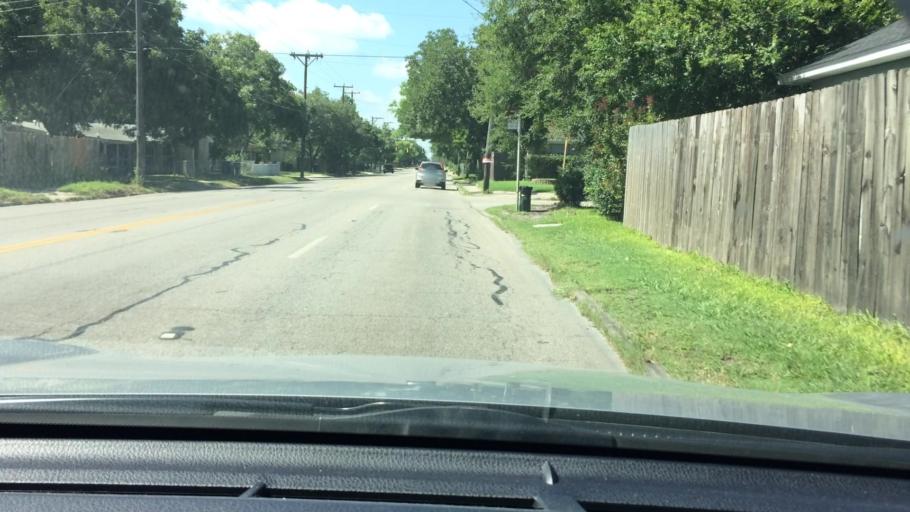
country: US
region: Texas
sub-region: Bexar County
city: Castle Hills
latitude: 29.5089
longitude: -98.5352
